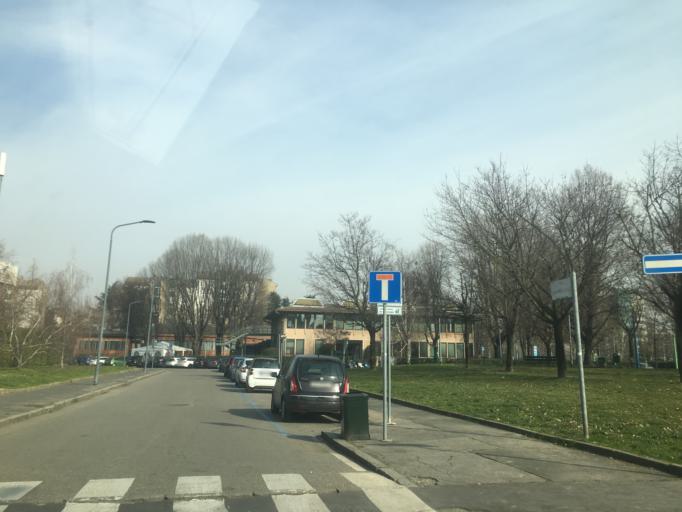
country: IT
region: Lombardy
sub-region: Citta metropolitana di Milano
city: Bresso
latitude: 45.5188
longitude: 9.2065
